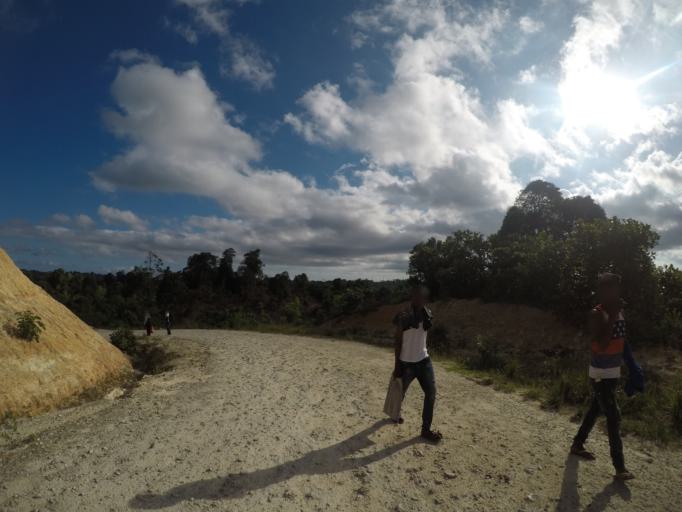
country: TZ
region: Pemba South
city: Mtambile
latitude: -5.3519
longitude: 39.7032
